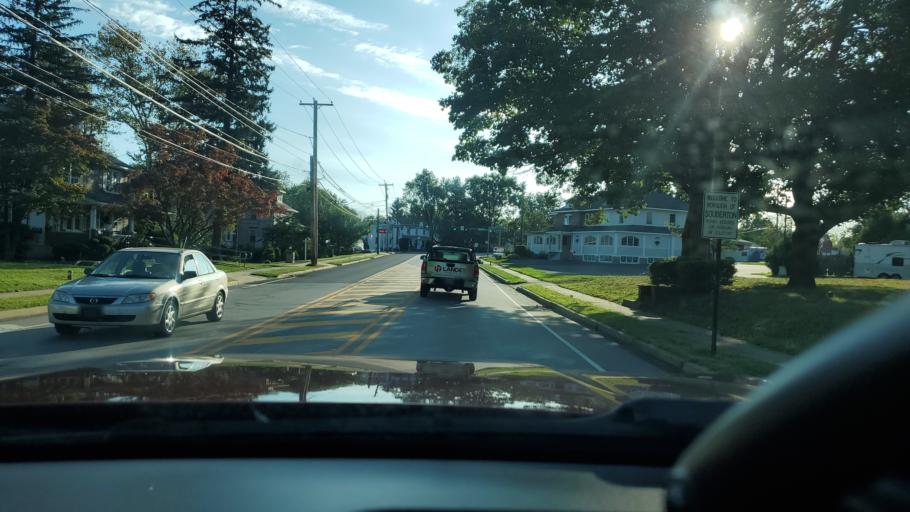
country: US
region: Pennsylvania
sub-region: Montgomery County
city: Telford
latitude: 40.3154
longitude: -75.3331
